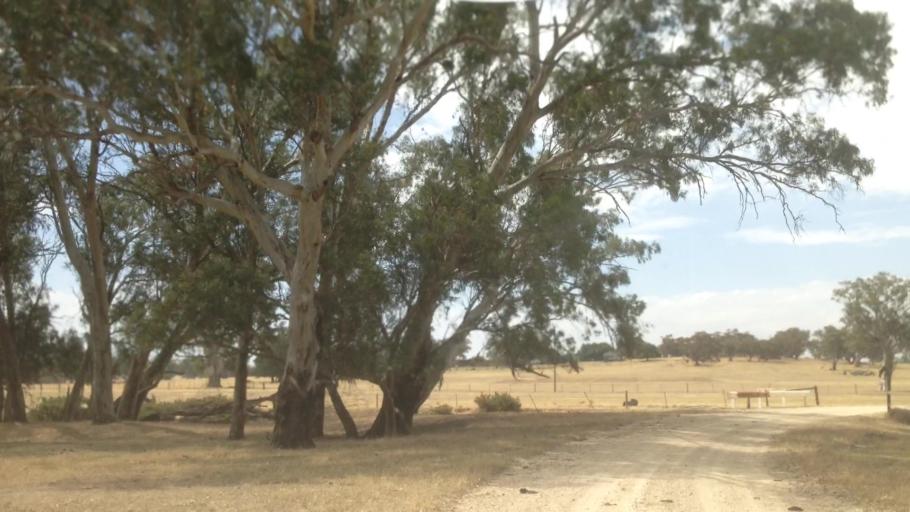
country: AU
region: South Australia
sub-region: Barossa
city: Williamstown
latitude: -34.7022
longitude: 138.9881
